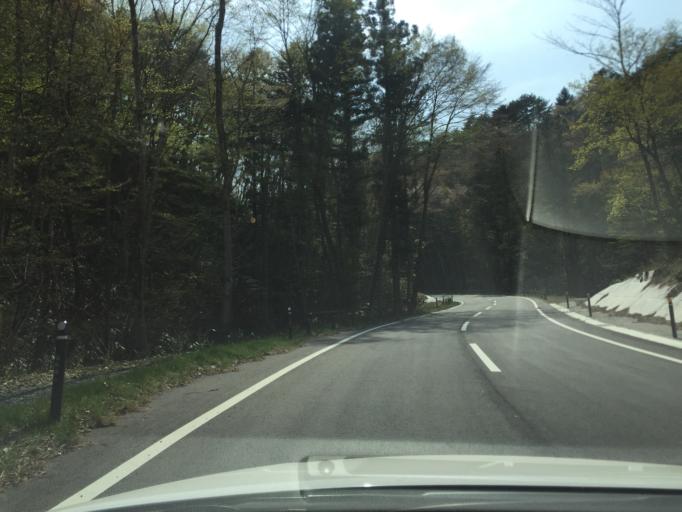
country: JP
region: Fukushima
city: Iwaki
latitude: 37.2502
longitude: 140.8502
